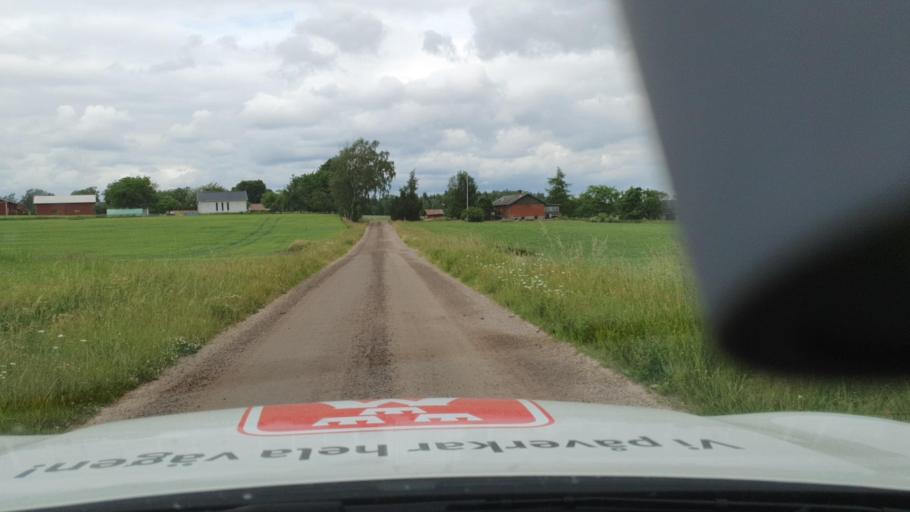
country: SE
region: Vaestra Goetaland
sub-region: Hjo Kommun
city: Hjo
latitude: 58.1949
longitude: 14.1755
